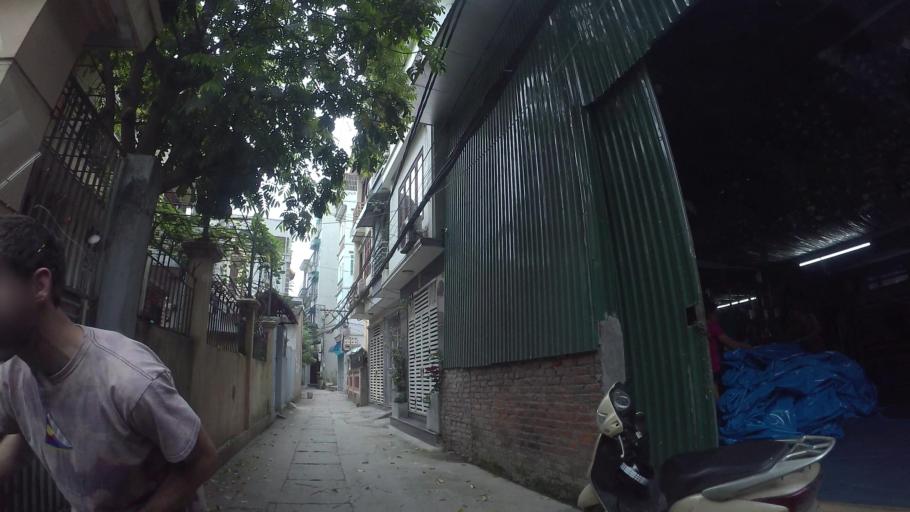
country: VN
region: Ha Noi
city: Van Dien
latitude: 20.9759
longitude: 105.8836
